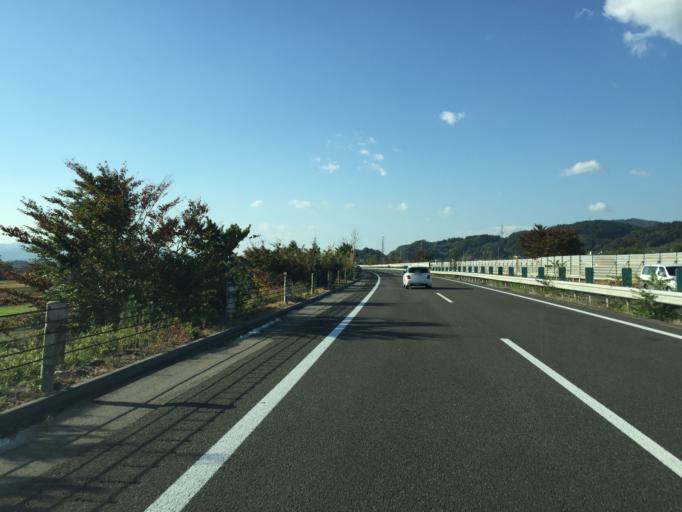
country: JP
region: Fukushima
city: Hobaramachi
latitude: 37.8754
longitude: 140.5250
